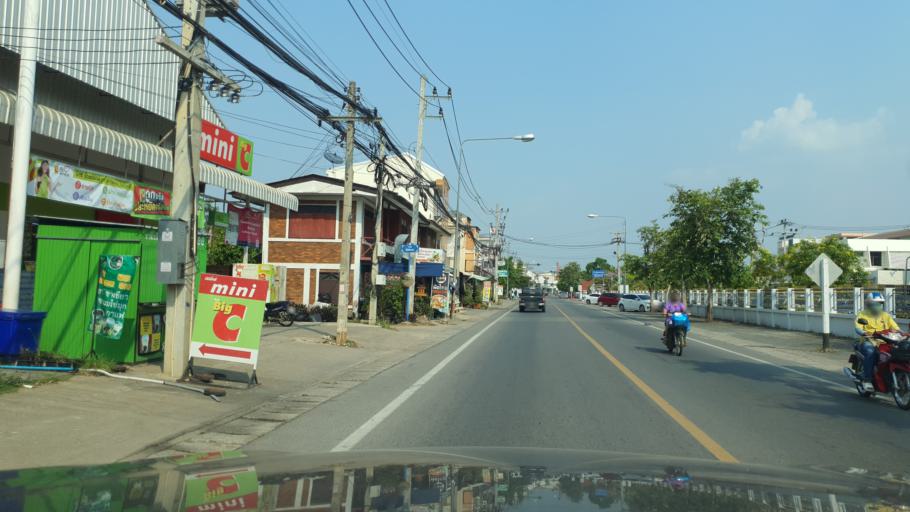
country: TH
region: Lamphun
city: Lamphun
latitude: 18.5835
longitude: 98.9940
